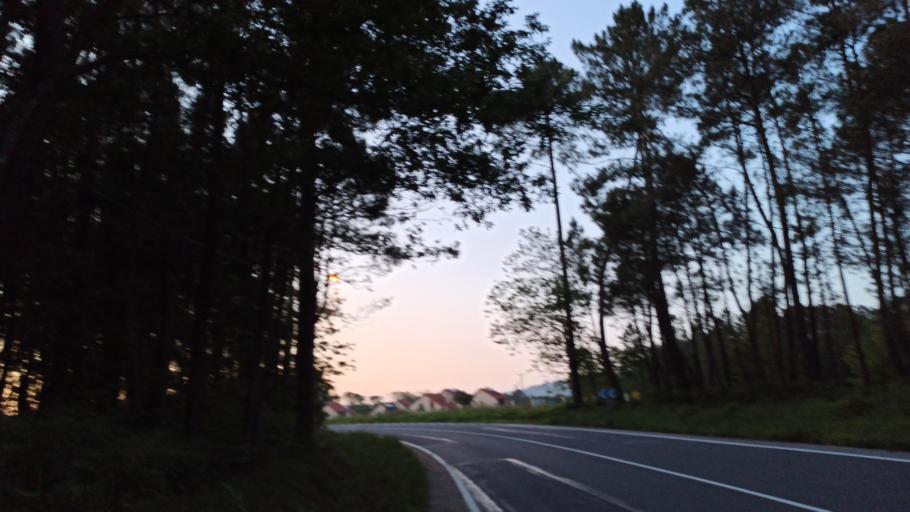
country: ES
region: Galicia
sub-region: Provincia da Coruna
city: Negreira
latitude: 42.9030
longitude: -8.7359
